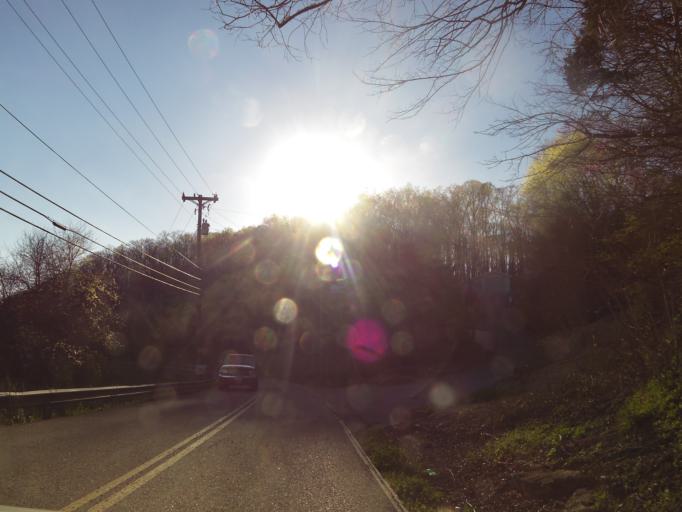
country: US
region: Tennessee
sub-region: Sevier County
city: Seymour
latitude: 35.9631
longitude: -83.7704
